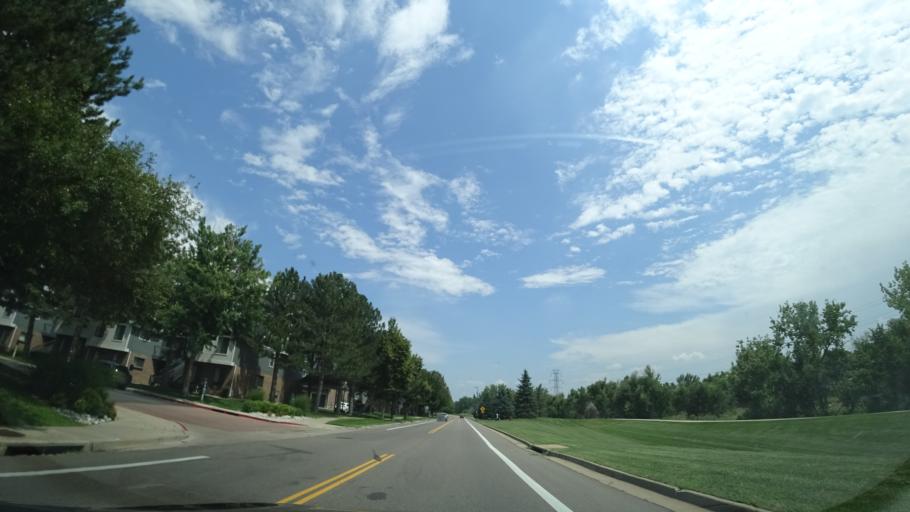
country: US
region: Colorado
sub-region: Jefferson County
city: Lakewood
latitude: 39.7014
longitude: -105.0790
